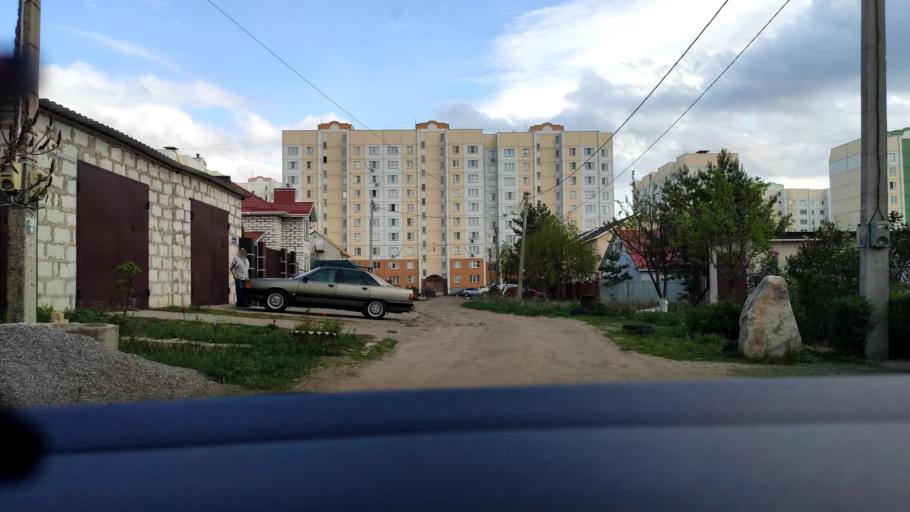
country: RU
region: Voronezj
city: Shilovo
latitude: 51.5640
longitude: 39.1121
